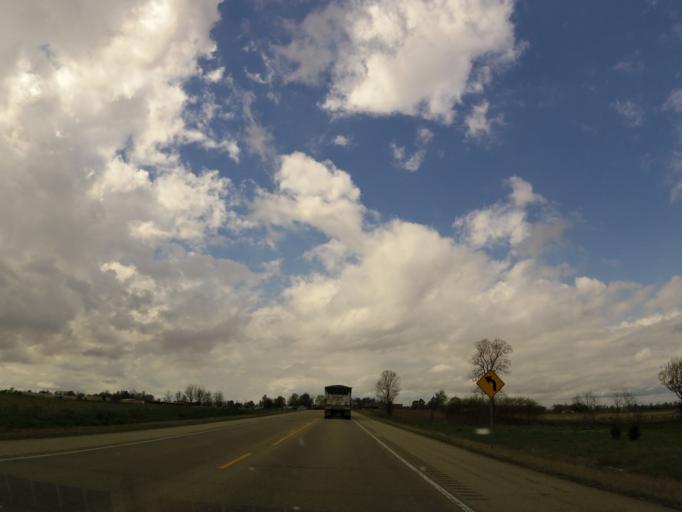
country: US
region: Arkansas
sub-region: Clay County
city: Corning
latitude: 36.4580
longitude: -90.5805
